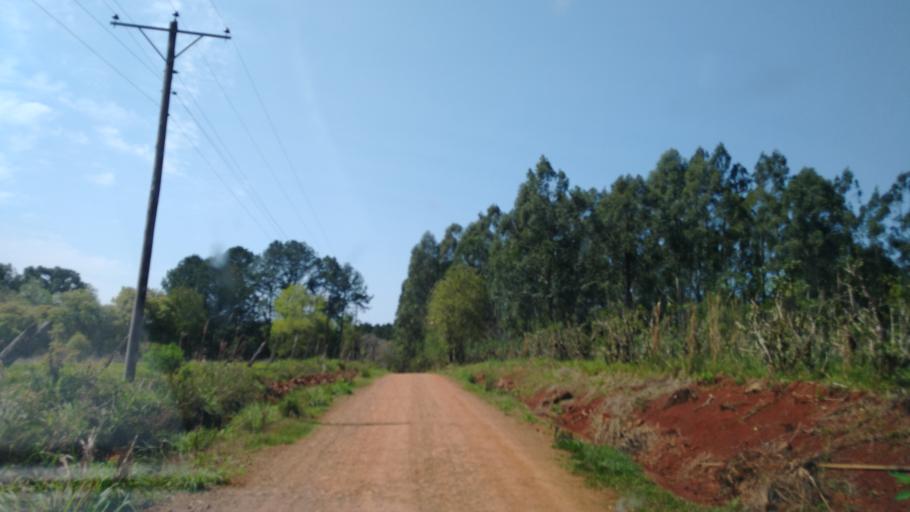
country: AR
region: Misiones
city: Capiovi
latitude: -26.9415
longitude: -55.0608
